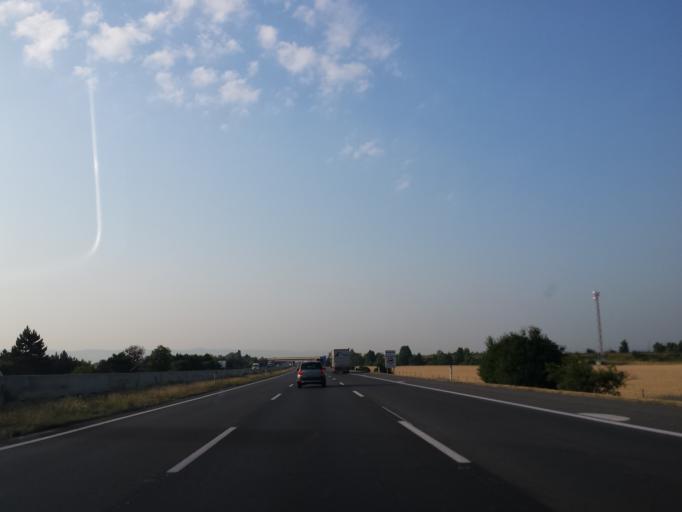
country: AT
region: Lower Austria
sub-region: Politischer Bezirk Wiener Neustadt
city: Weikersdorf am Steinfelde
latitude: 47.8232
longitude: 16.1883
